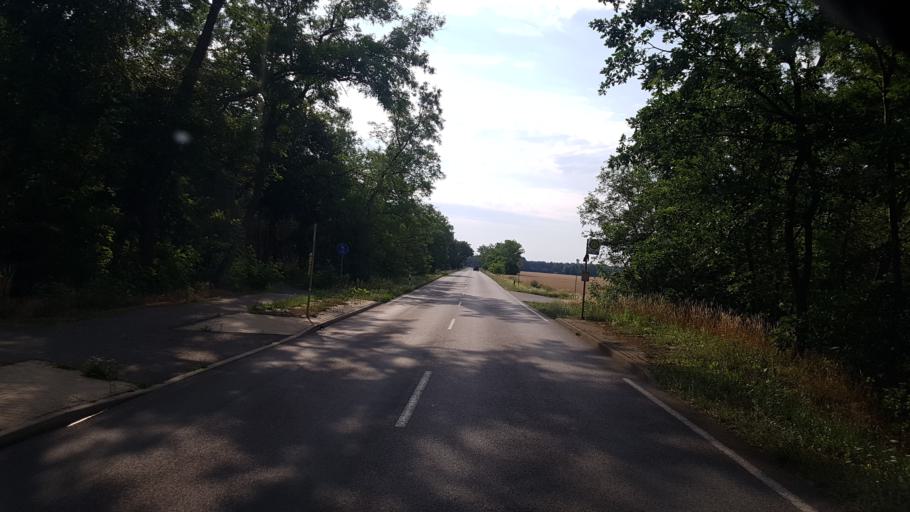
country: DE
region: Brandenburg
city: Baruth
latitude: 52.0553
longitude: 13.5685
